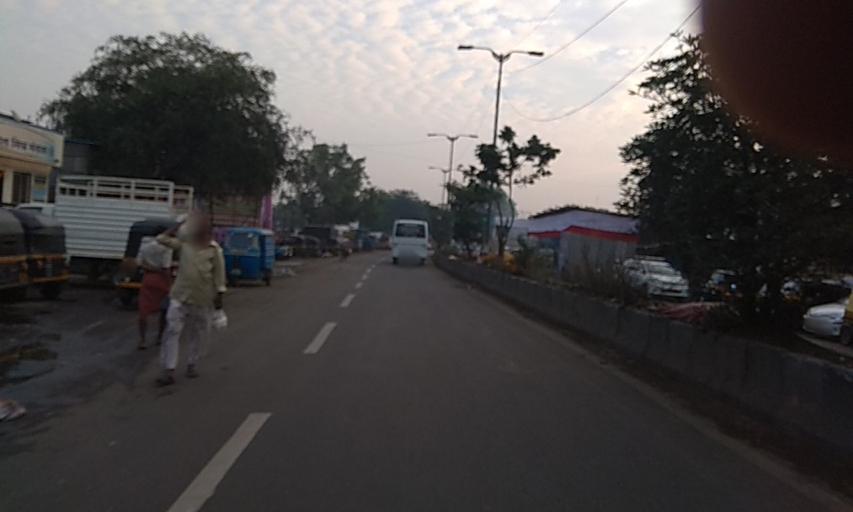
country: IN
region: Maharashtra
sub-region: Pune Division
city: Pune
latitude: 18.5263
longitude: 73.8612
